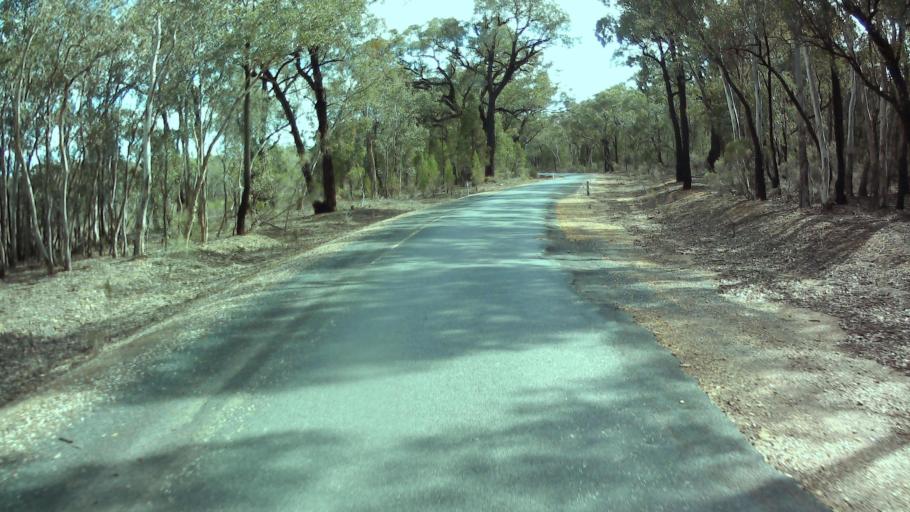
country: AU
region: New South Wales
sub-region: Weddin
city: Grenfell
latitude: -33.8579
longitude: 148.2156
